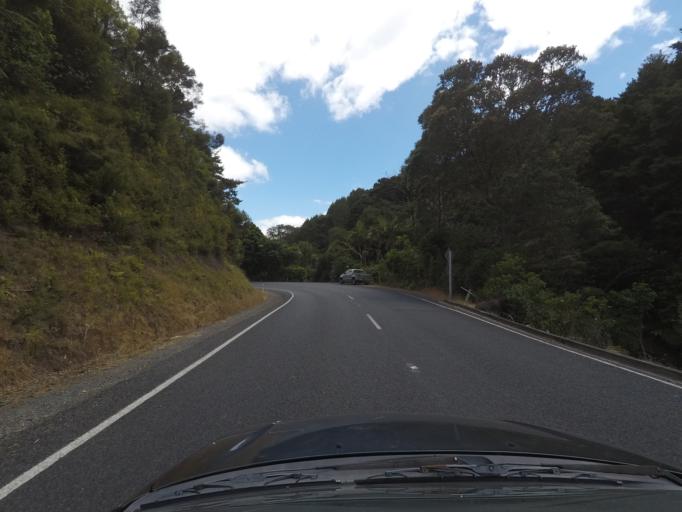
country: NZ
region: Northland
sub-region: Whangarei
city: Ruakaka
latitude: -36.0332
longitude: 174.5103
